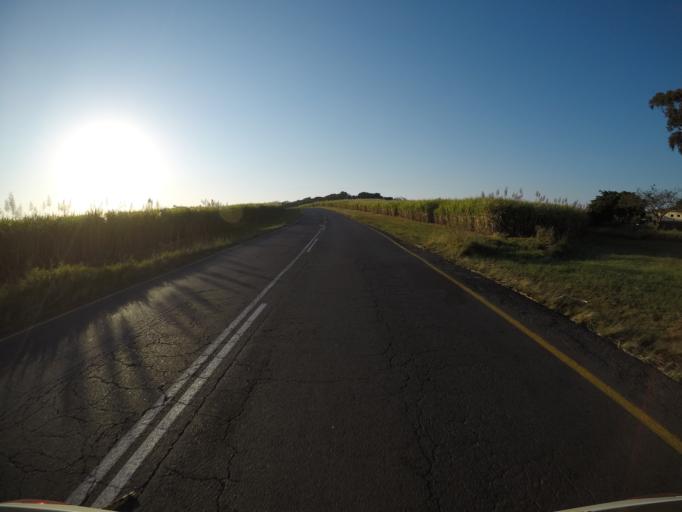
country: ZA
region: KwaZulu-Natal
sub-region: uThungulu District Municipality
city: eSikhawini
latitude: -28.9493
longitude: 31.6943
